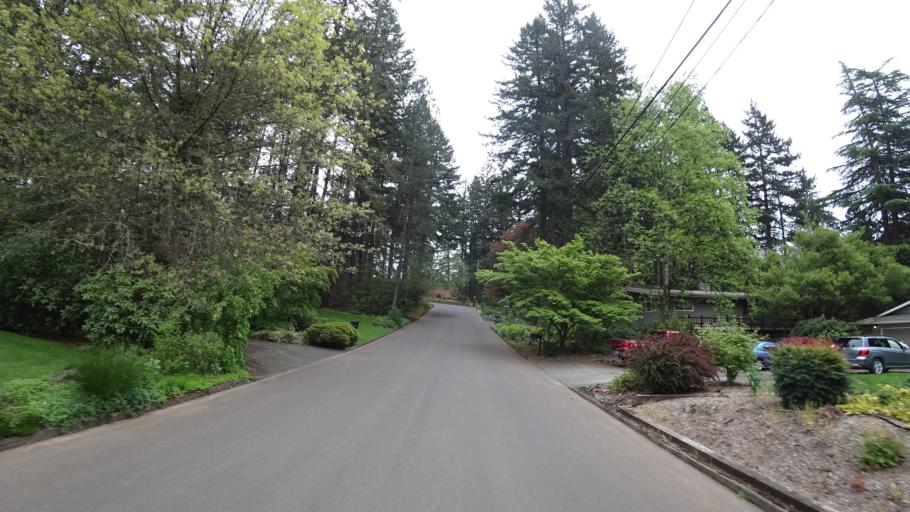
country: US
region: Oregon
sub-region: Washington County
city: Beaverton
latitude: 45.4628
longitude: -122.8185
